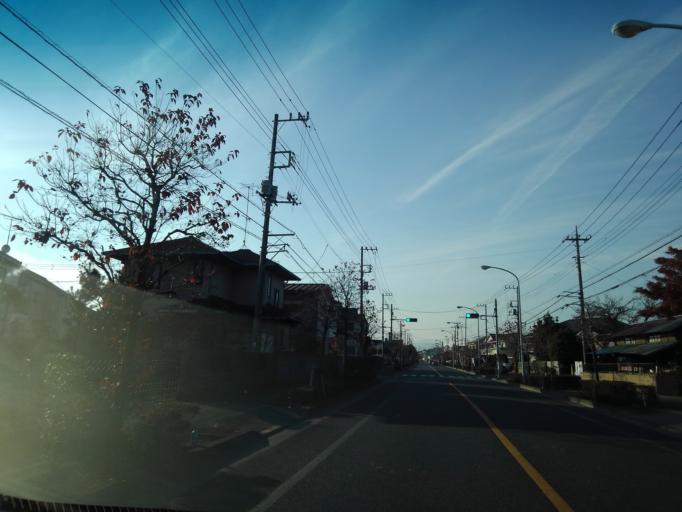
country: JP
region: Tokyo
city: Fussa
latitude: 35.7924
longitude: 139.3550
